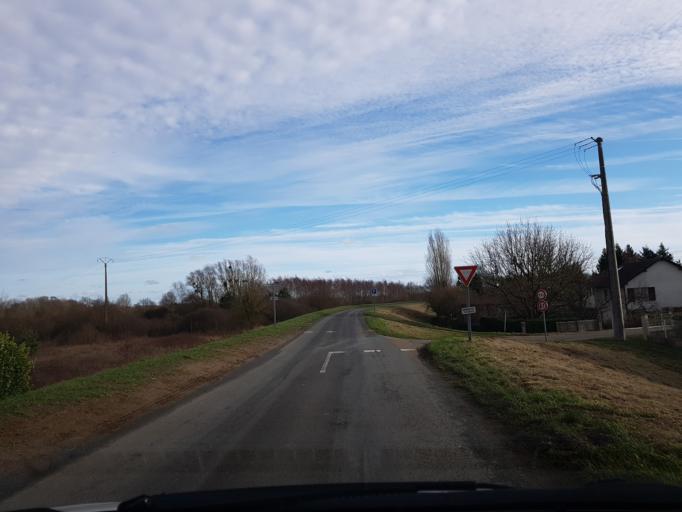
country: FR
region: Centre
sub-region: Departement du Loiret
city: Saint-Jean-de-Braye
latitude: 47.8957
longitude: 1.9635
